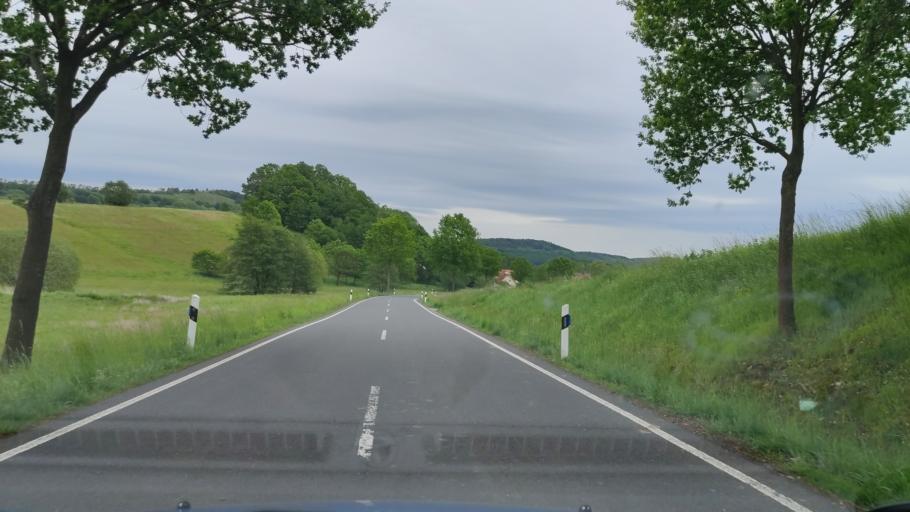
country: DE
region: Lower Saxony
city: Hardegsen
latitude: 51.6933
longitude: 9.7973
